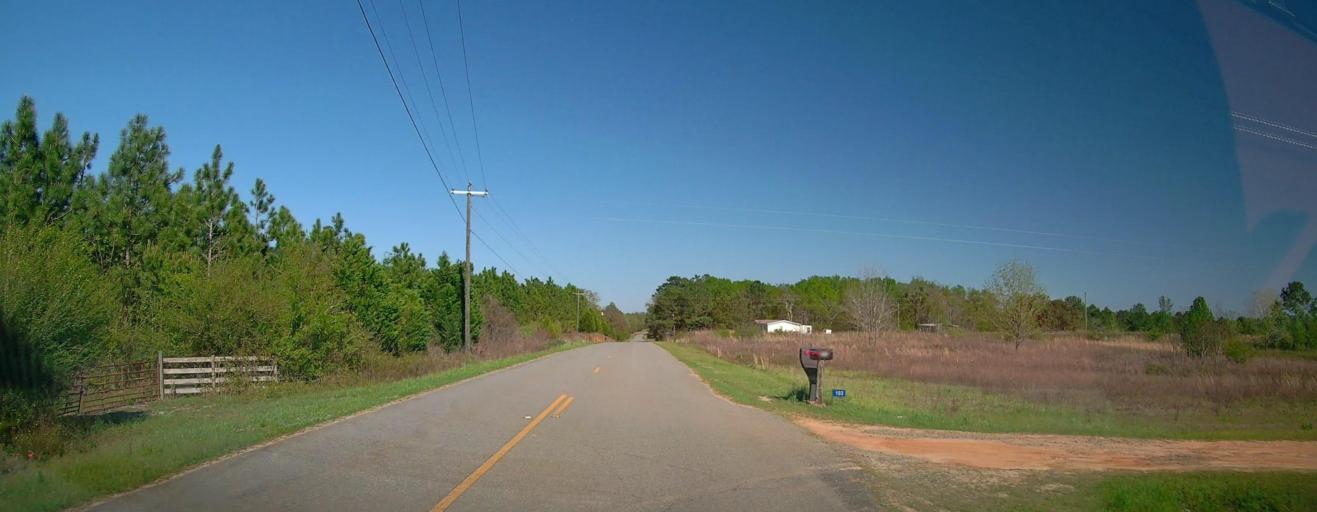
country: US
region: Georgia
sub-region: Pulaski County
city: Hawkinsville
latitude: 32.2404
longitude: -83.5204
